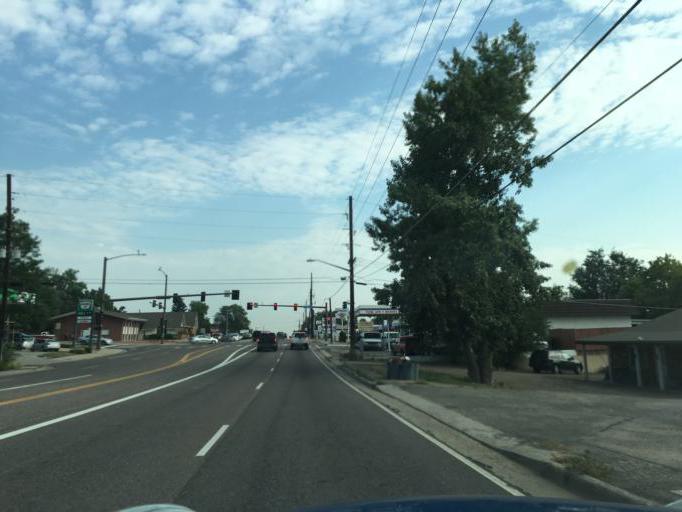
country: US
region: Colorado
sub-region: Jefferson County
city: Wheat Ridge
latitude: 39.7465
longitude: -105.1095
